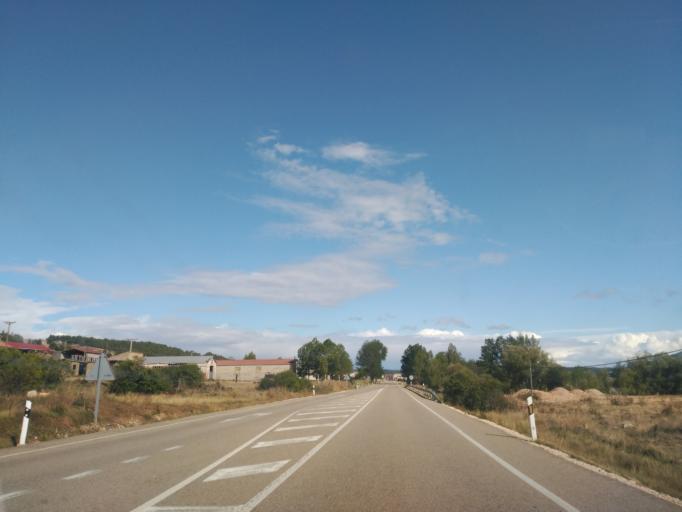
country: ES
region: Castille and Leon
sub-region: Provincia de Burgos
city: Hontoria del Pinar
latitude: 41.8515
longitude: -3.1756
